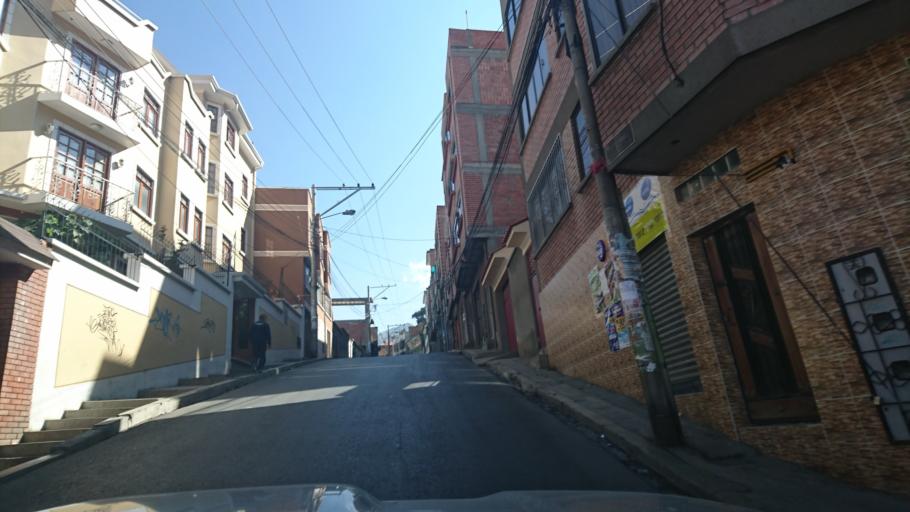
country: BO
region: La Paz
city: La Paz
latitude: -16.4836
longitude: -68.1161
